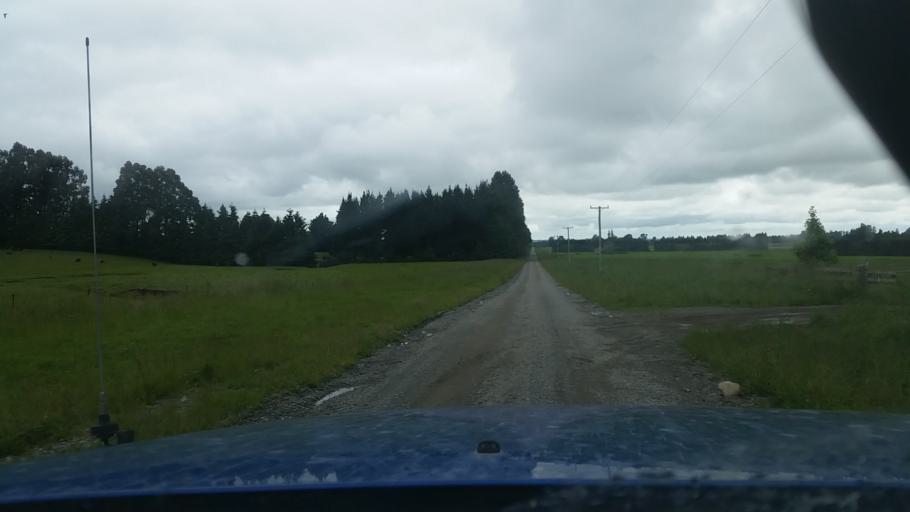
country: NZ
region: Canterbury
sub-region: Ashburton District
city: Methven
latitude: -43.6952
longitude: 171.4098
